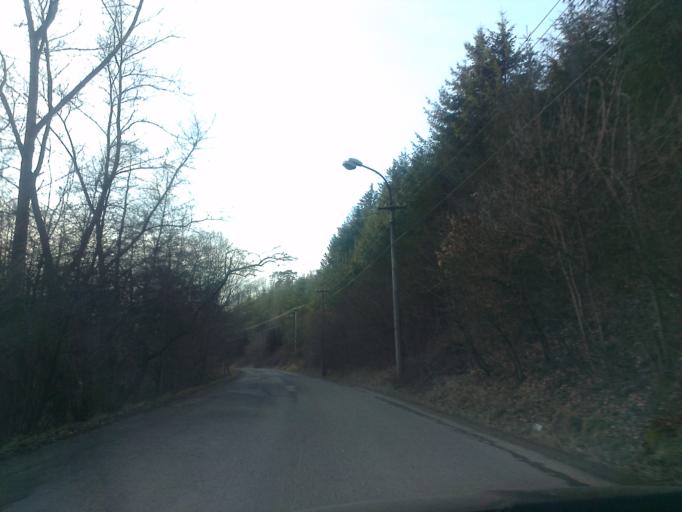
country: CZ
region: South Moravian
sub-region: Okres Blansko
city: Jedovnice
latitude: 49.2932
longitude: 16.7530
